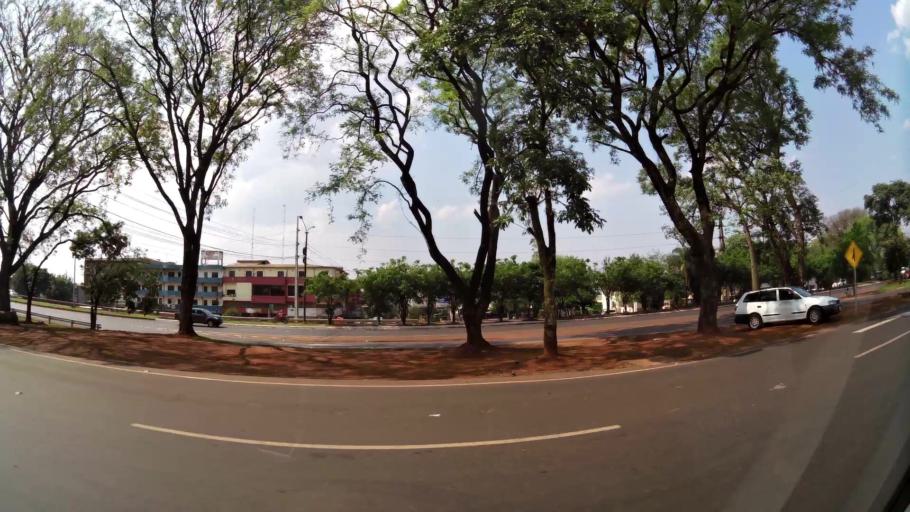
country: PY
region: Alto Parana
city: Ciudad del Este
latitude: -25.5081
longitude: -54.6364
